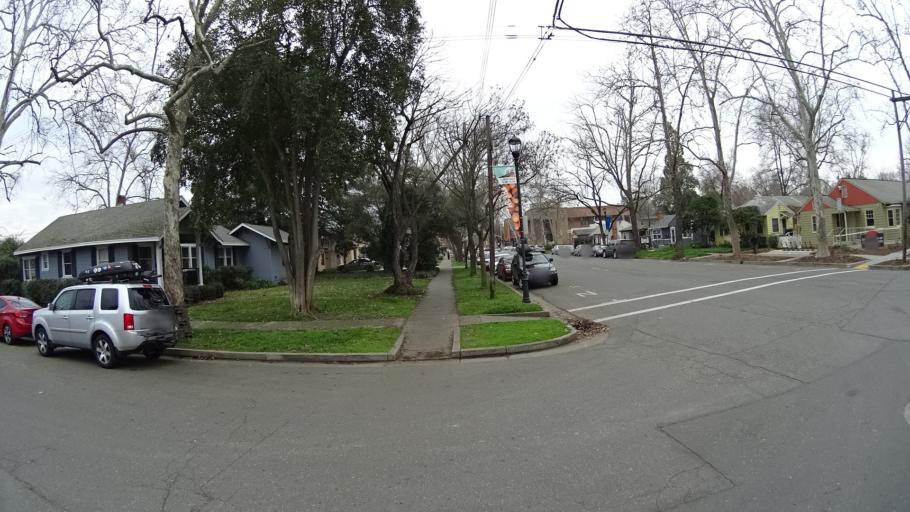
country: US
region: California
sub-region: Yolo County
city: Davis
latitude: 38.5489
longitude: -121.7403
